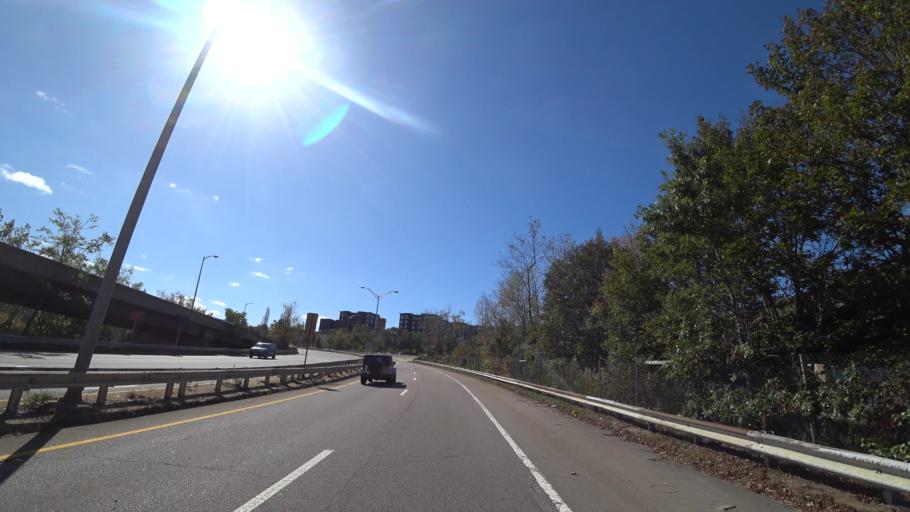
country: US
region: Massachusetts
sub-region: Norfolk County
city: Braintree
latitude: 42.2325
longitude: -71.0106
